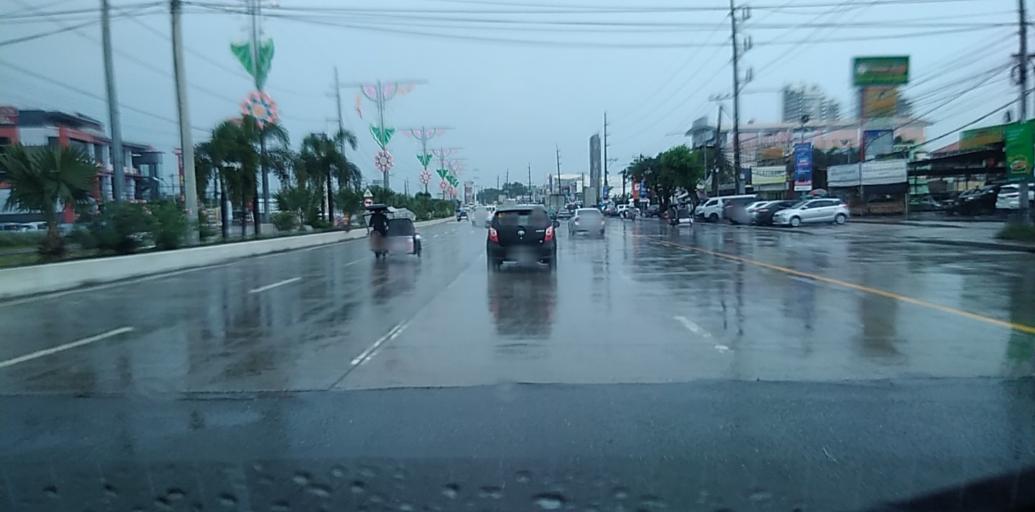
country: PH
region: Central Luzon
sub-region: Province of Pampanga
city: Del Pilar
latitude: 15.0452
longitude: 120.6900
